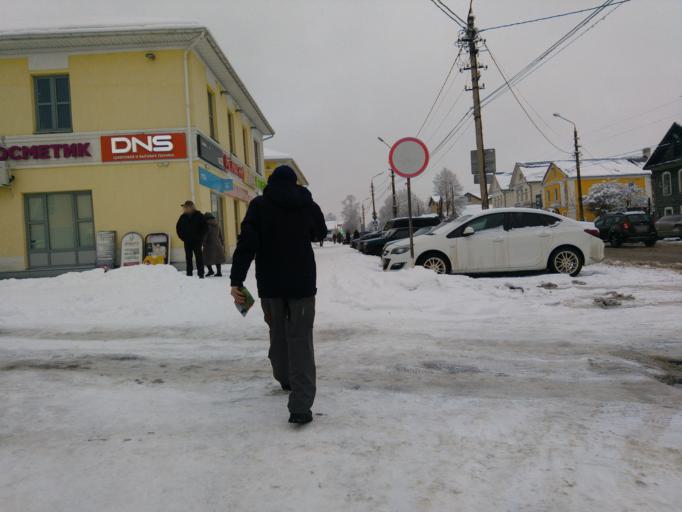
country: RU
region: Tverskaya
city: Torzhok
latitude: 57.0446
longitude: 34.9699
